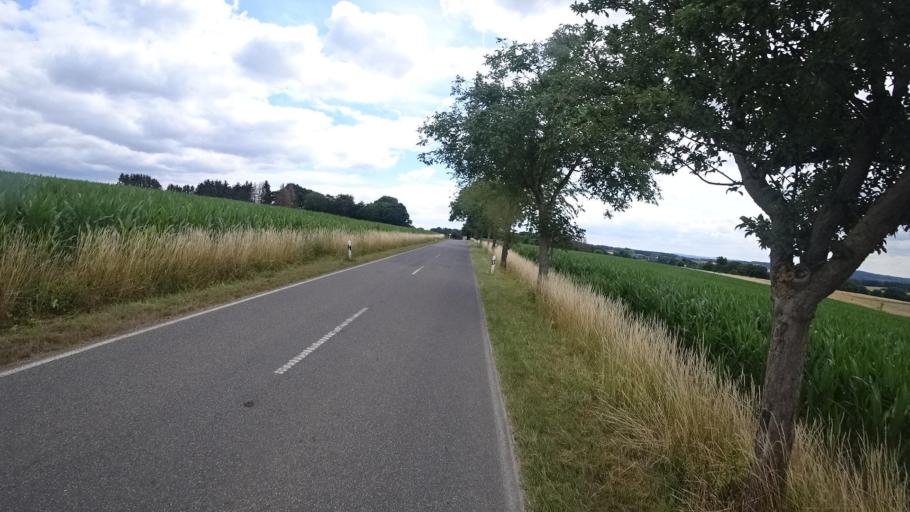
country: DE
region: Rheinland-Pfalz
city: Weyerbusch
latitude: 50.7182
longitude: 7.5391
